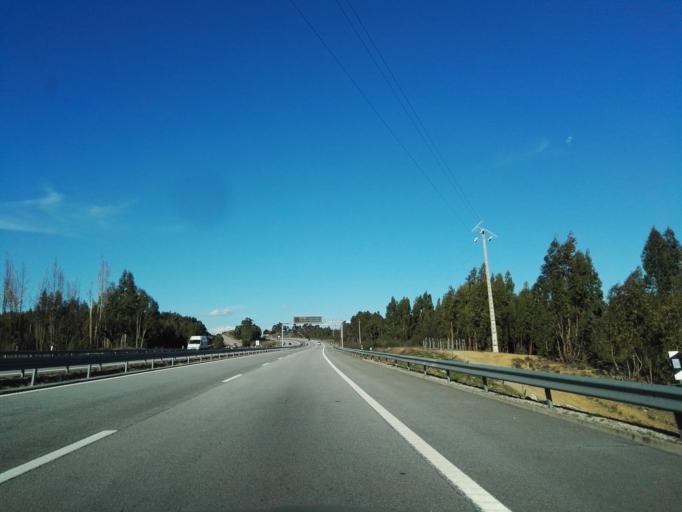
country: PT
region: Portalegre
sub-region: Nisa
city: Nisa
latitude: 39.7098
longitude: -7.6936
